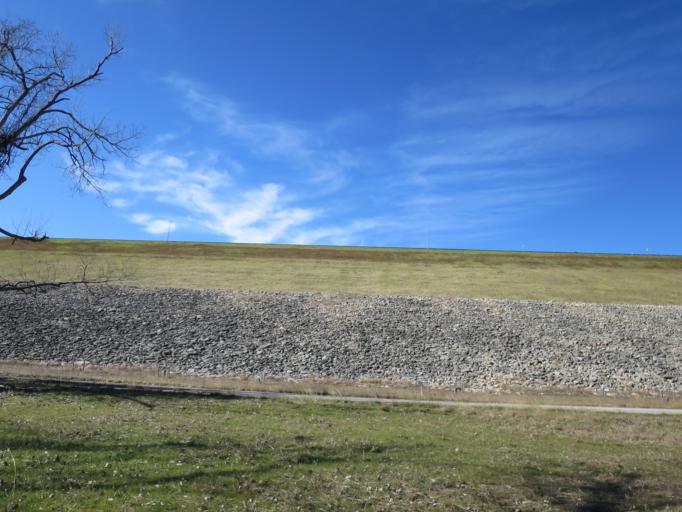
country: US
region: Texas
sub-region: Bell County
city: Belton
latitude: 31.0247
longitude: -97.5276
